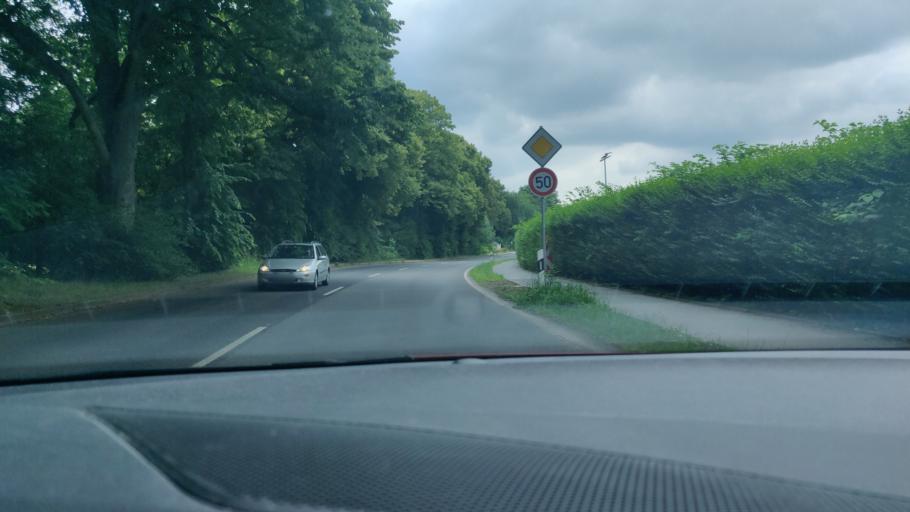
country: DE
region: North Rhine-Westphalia
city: Haan
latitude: 51.2218
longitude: 7.0534
